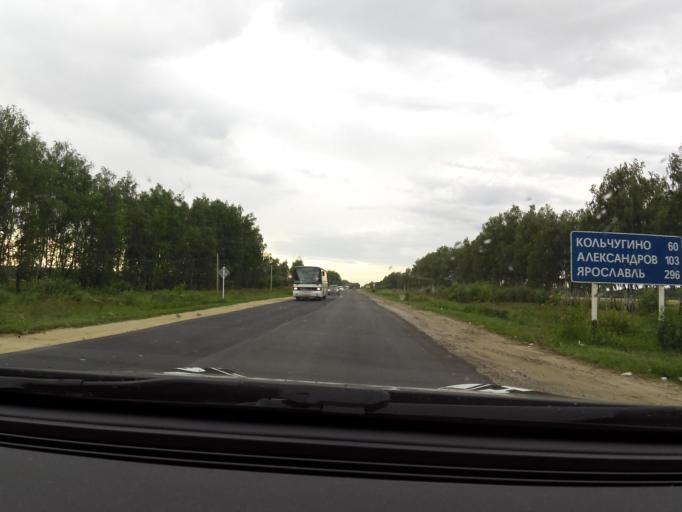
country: RU
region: Vladimir
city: Vorsha
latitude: 56.0622
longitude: 40.1222
